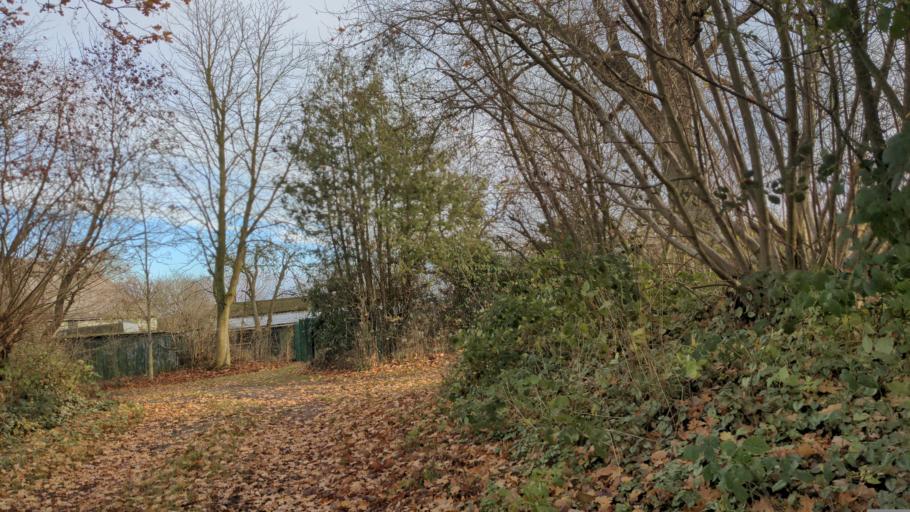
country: DE
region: Schleswig-Holstein
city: Neustadt in Holstein
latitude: 54.0881
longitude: 10.7931
